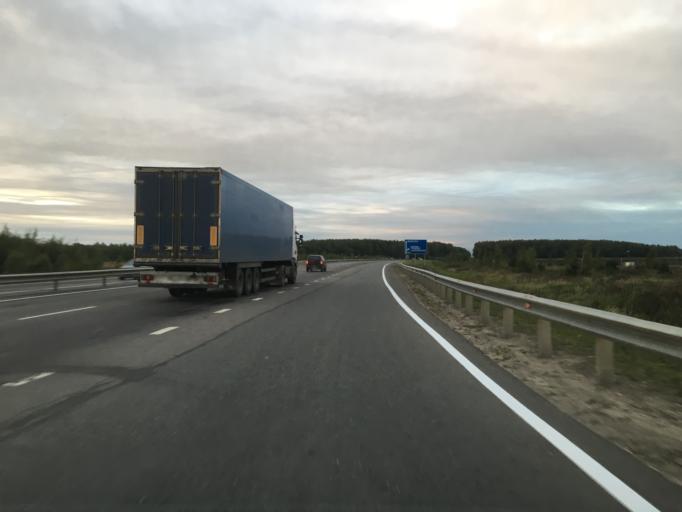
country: RU
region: Kaluga
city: Kaluga
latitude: 54.5687
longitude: 36.3347
